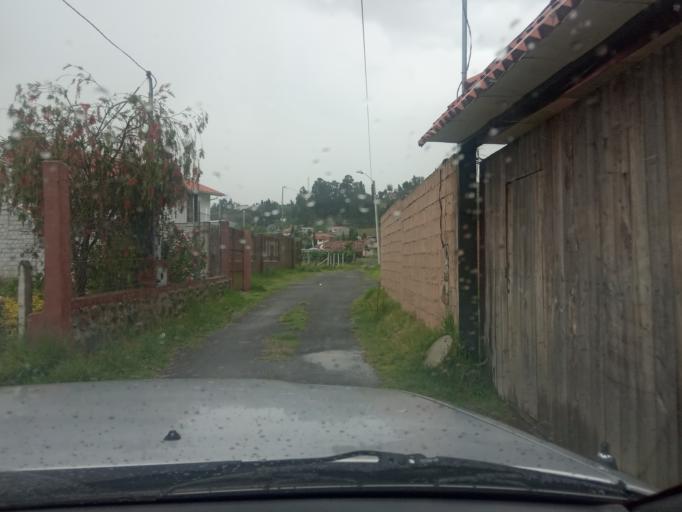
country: EC
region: Azuay
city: Llacao
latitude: -2.8675
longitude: -78.9438
